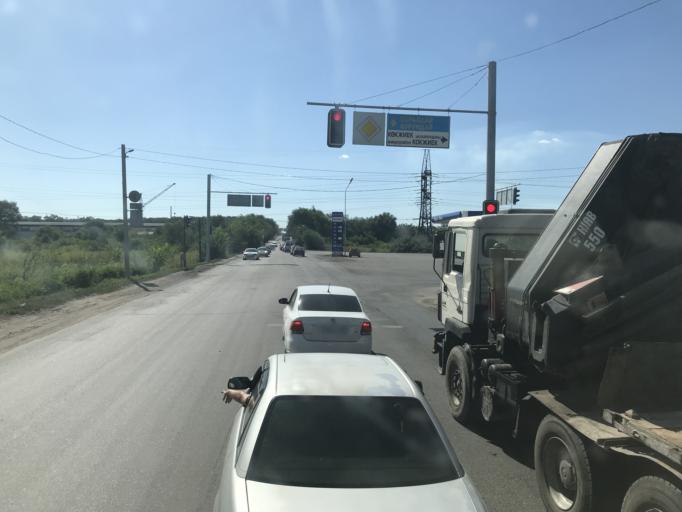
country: KZ
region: Almaty Oblysy
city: Pervomayskiy
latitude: 43.3548
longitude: 76.9154
